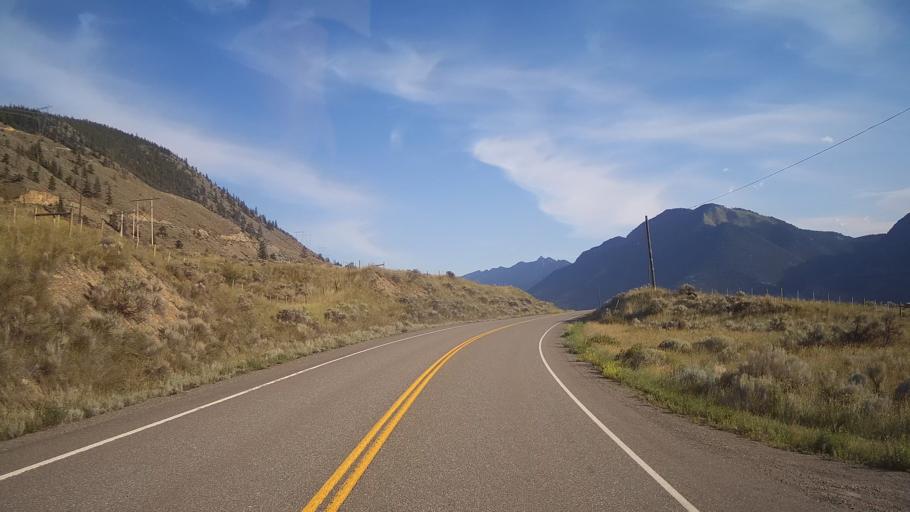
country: CA
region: British Columbia
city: Lillooet
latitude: 50.8525
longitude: -121.8620
